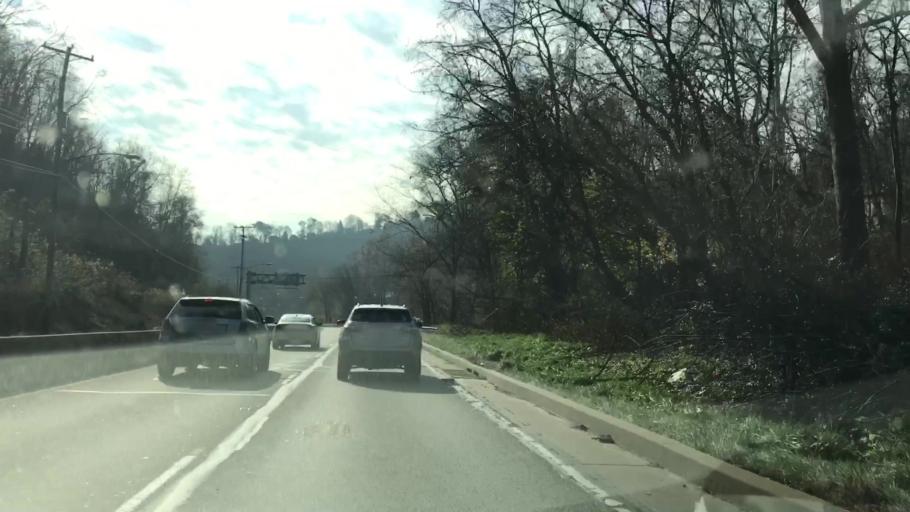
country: US
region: Pennsylvania
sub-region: Allegheny County
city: Mount Oliver
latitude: 40.4200
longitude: -80.0153
